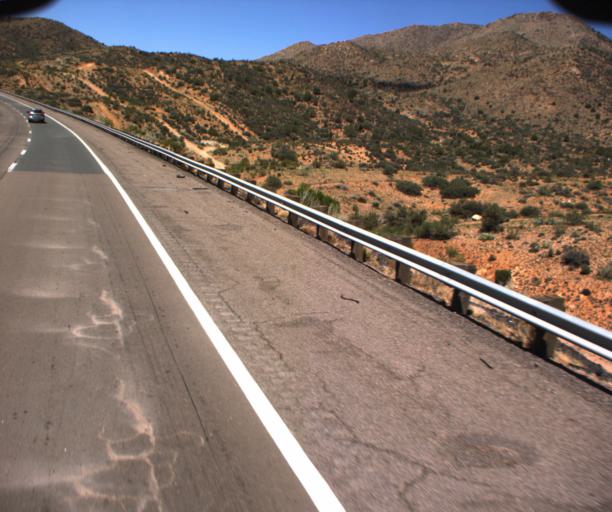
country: US
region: Arizona
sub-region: Mohave County
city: Peach Springs
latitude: 35.1713
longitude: -113.5211
